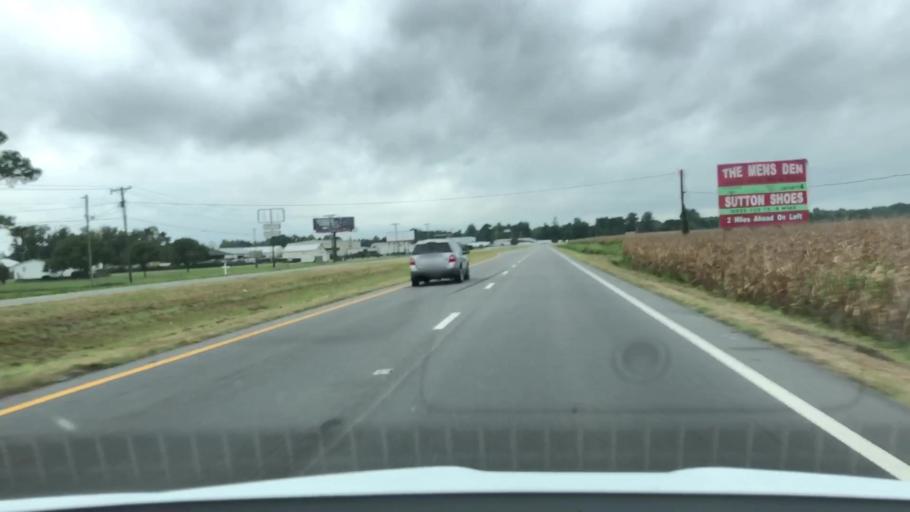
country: US
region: North Carolina
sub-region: Lenoir County
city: La Grange
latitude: 35.2679
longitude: -77.7338
